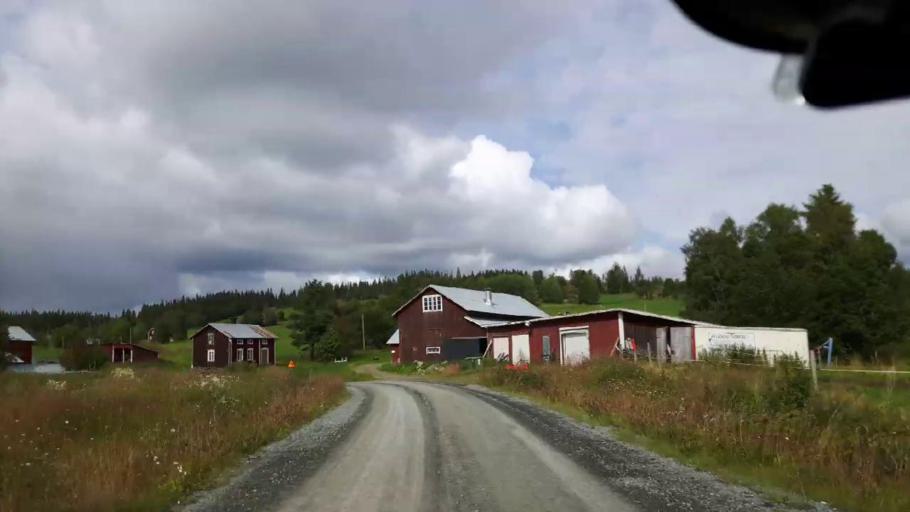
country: SE
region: Jaemtland
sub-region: Krokoms Kommun
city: Valla
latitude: 63.5772
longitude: 13.9041
